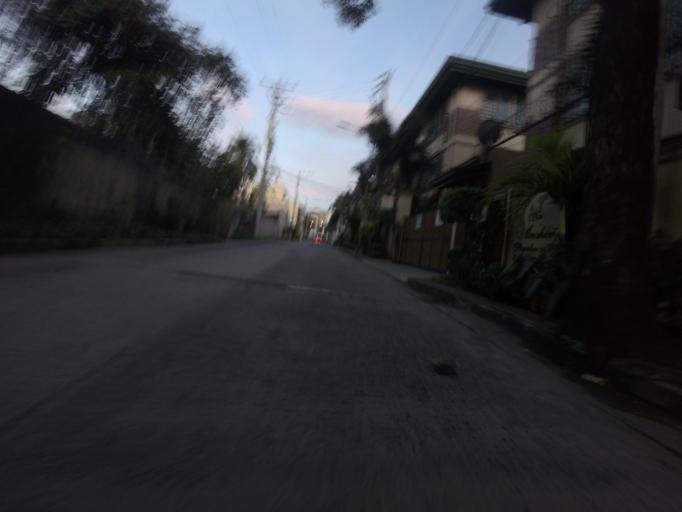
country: PH
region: Metro Manila
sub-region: San Juan
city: San Juan
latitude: 14.5942
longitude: 121.0387
